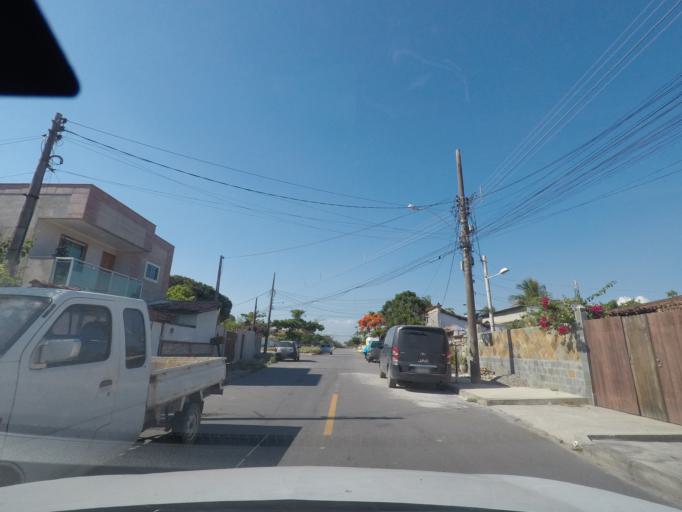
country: BR
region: Rio de Janeiro
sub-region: Marica
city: Marica
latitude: -22.9703
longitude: -42.9217
